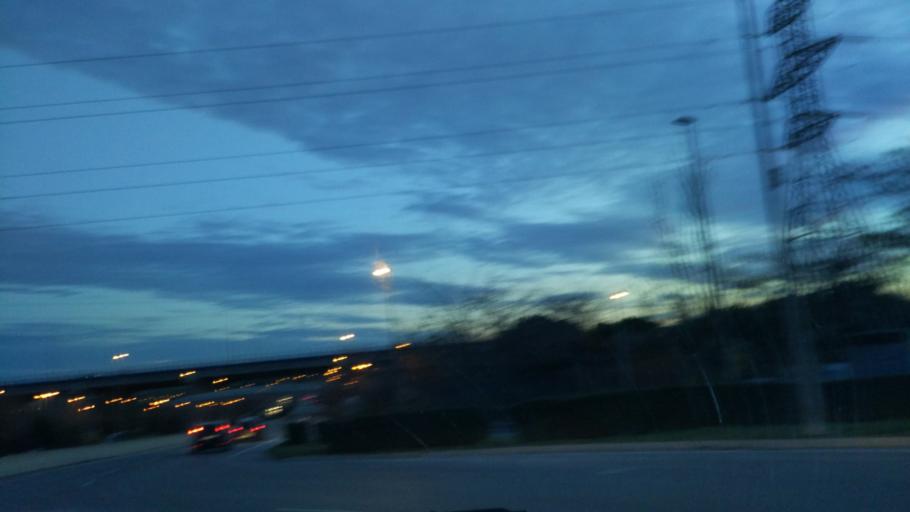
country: ES
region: Madrid
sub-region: Provincia de Madrid
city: Leganes
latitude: 40.3555
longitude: -3.7735
